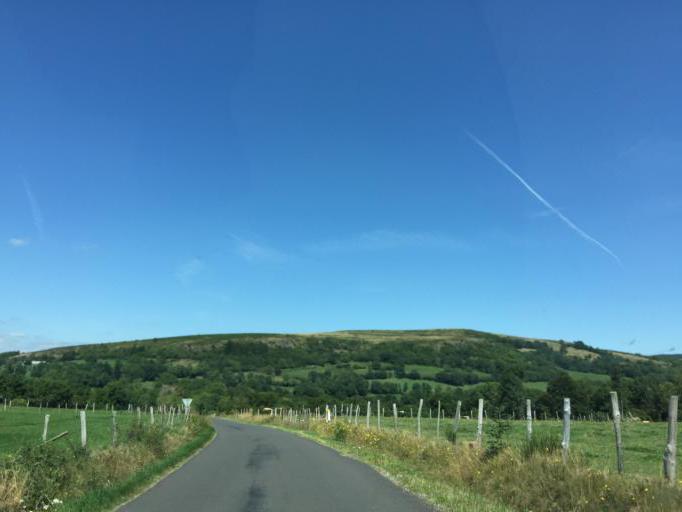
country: FR
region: Midi-Pyrenees
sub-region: Departement de l'Aveyron
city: Laguiole
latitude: 44.6535
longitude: 2.8515
